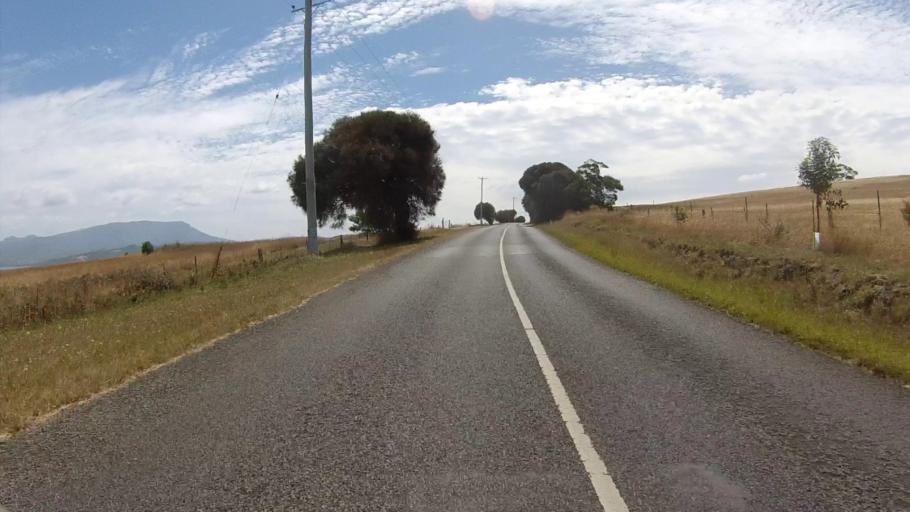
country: AU
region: Tasmania
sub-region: Kingborough
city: Taroona
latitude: -43.0046
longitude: 147.4033
